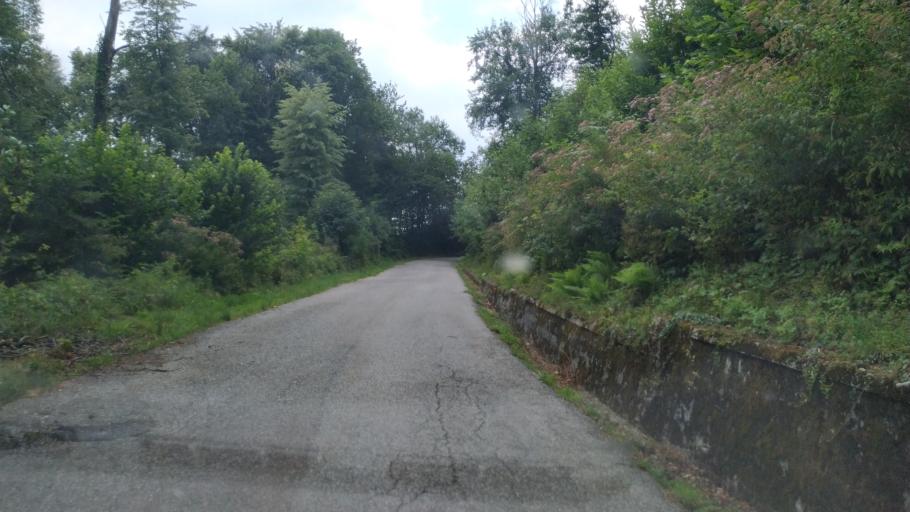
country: IT
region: Piedmont
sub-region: Provincia di Vercelli
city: Varallo
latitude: 45.7996
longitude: 8.2515
